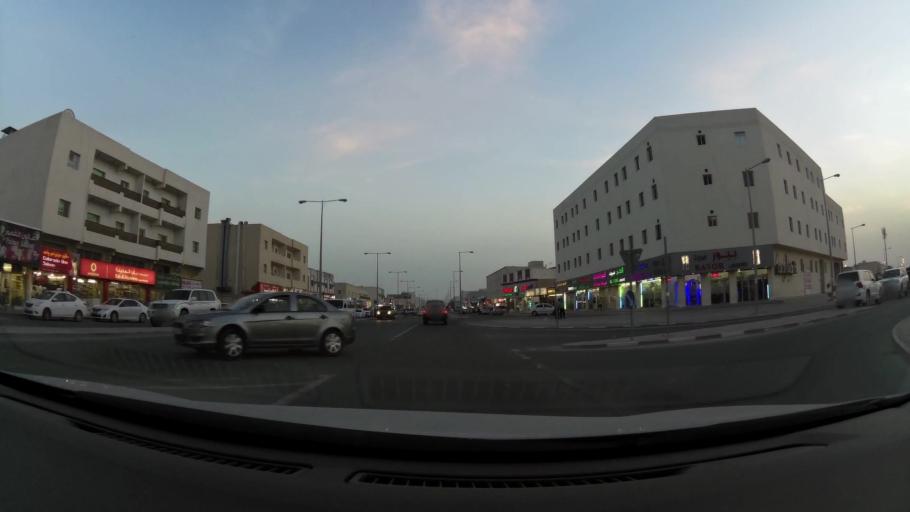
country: QA
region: Al Wakrah
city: Al Wakrah
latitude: 25.1559
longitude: 51.5993
